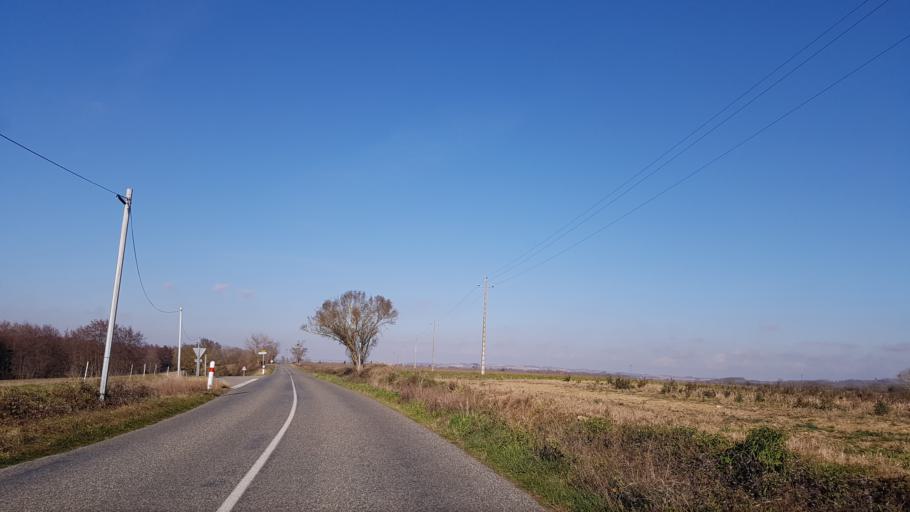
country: FR
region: Midi-Pyrenees
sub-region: Departement de l'Ariege
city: La Tour-du-Crieu
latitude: 43.1451
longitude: 1.7044
